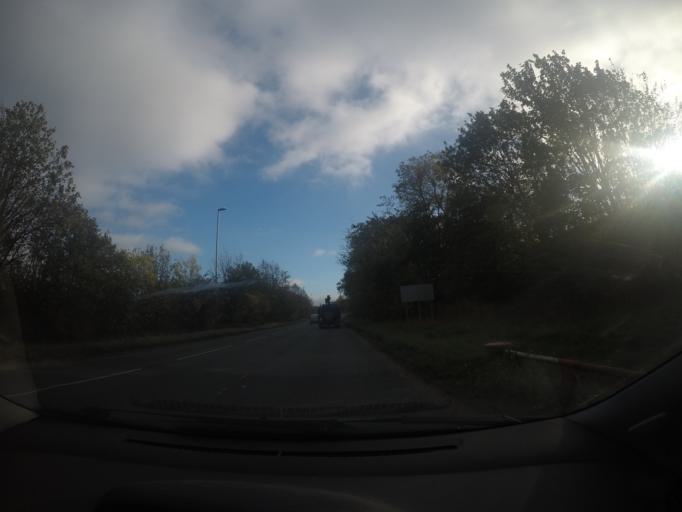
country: GB
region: England
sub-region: City and Borough of Leeds
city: Lofthouse
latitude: 53.7685
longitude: -1.5148
